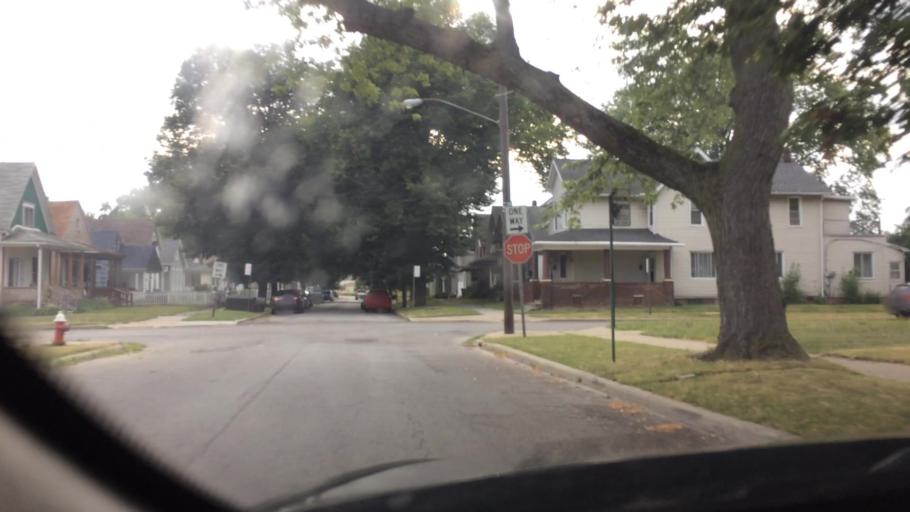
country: US
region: Ohio
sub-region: Wood County
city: Rossford
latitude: 41.6298
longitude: -83.5645
